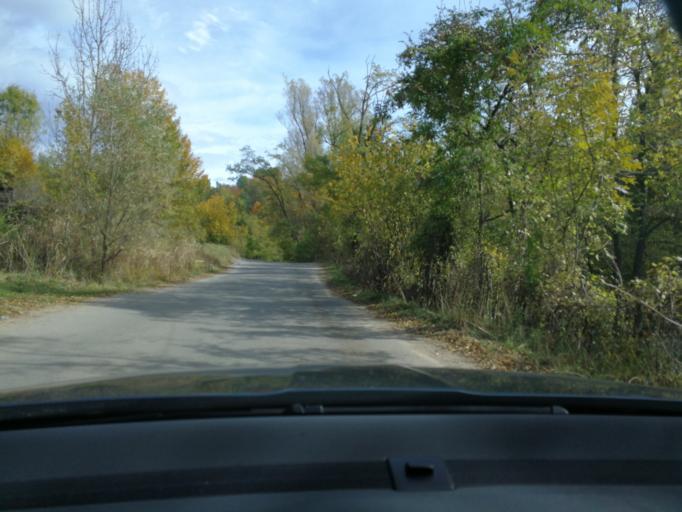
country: RO
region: Prahova
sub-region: Comuna Brebu
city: Pietriceaua
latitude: 45.2059
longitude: 25.7954
